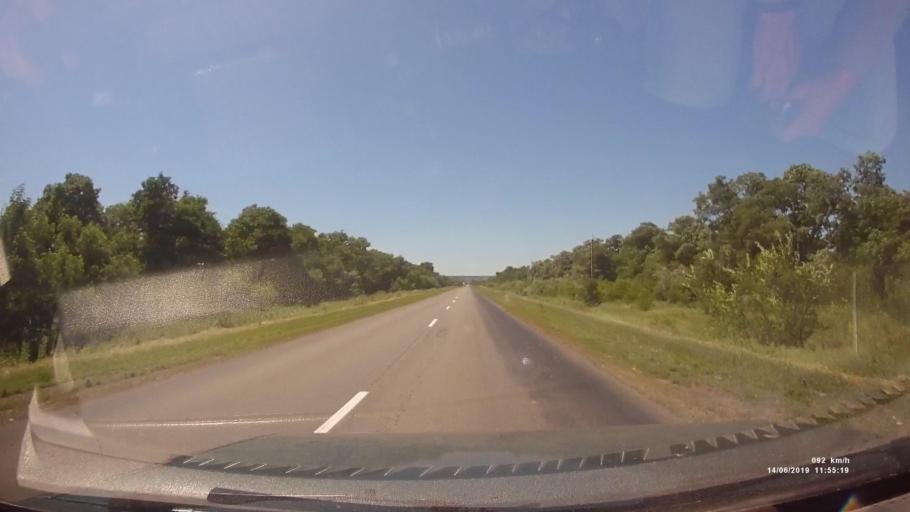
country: RU
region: Rostov
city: Kazanskaya
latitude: 49.8115
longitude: 41.1790
